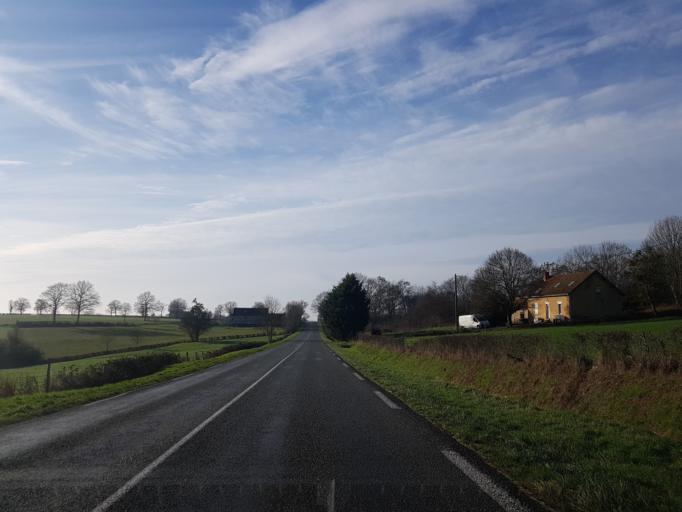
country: FR
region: Bourgogne
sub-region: Departement de Saone-et-Loire
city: Bourbon-Lancy
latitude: 46.6067
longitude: 3.8691
